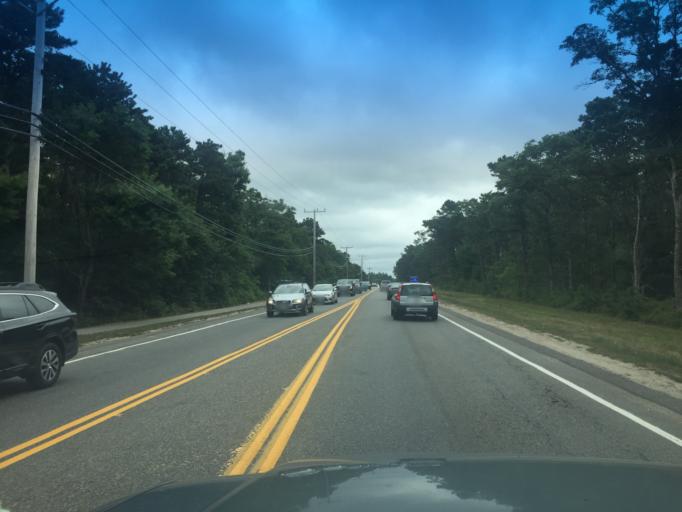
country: US
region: Massachusetts
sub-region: Barnstable County
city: Mashpee
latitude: 41.6170
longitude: -70.5078
